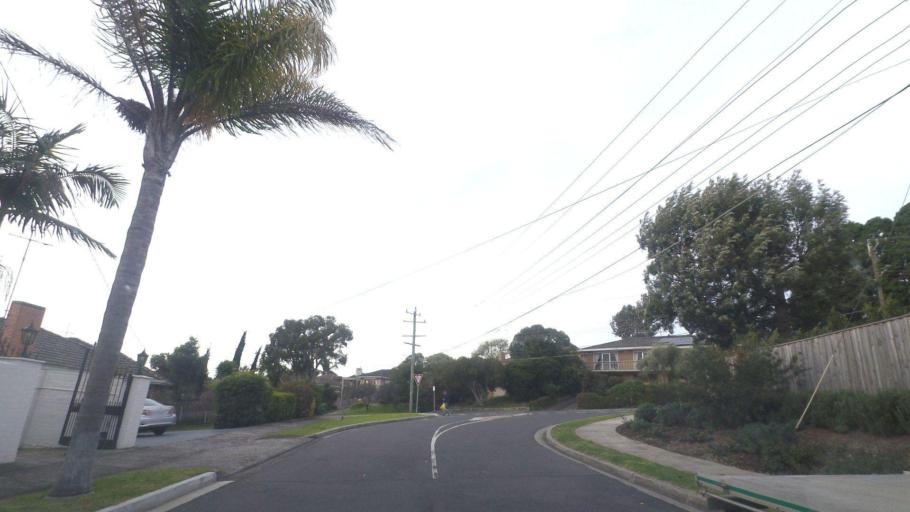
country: AU
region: Victoria
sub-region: Manningham
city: Bulleen
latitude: -37.7729
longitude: 145.0943
